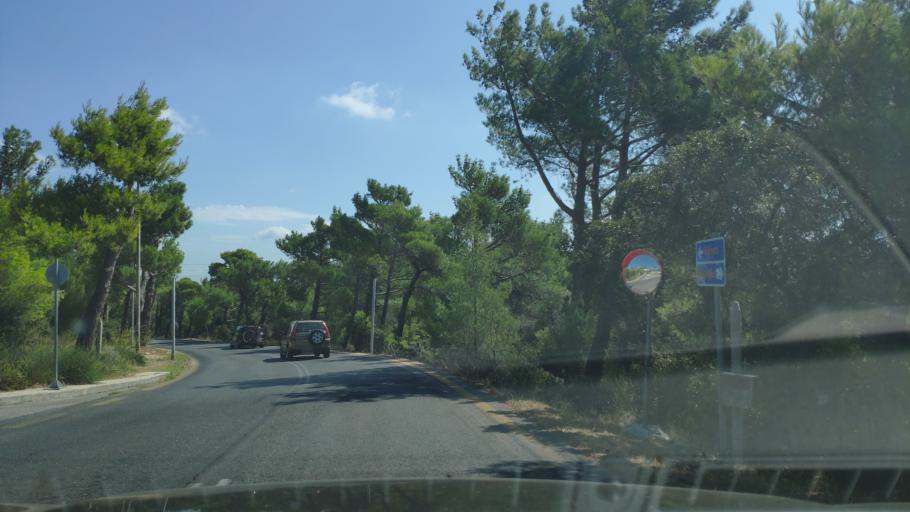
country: GR
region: Attica
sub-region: Nomarchia Anatolikis Attikis
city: Thrakomakedones
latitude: 38.1364
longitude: 23.7421
